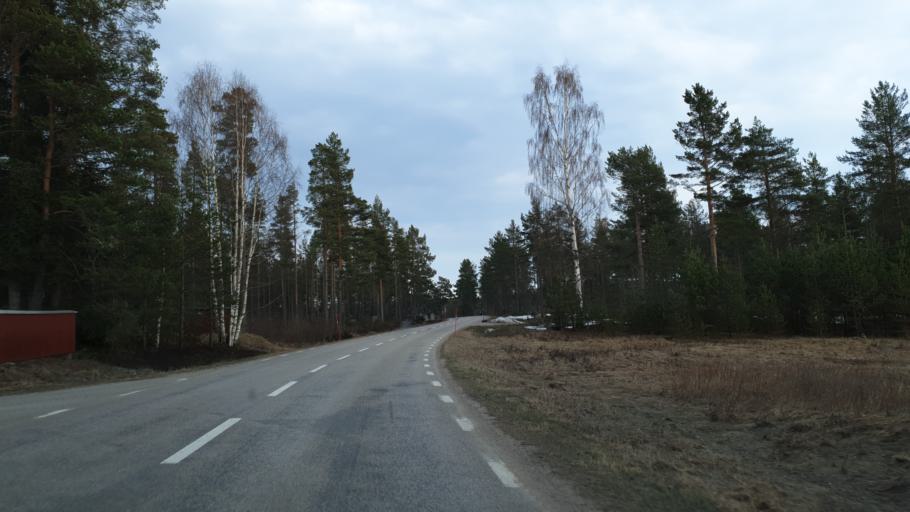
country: SE
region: Gaevleborg
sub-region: Nordanstigs Kommun
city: Bergsjoe
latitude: 61.9717
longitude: 17.2974
